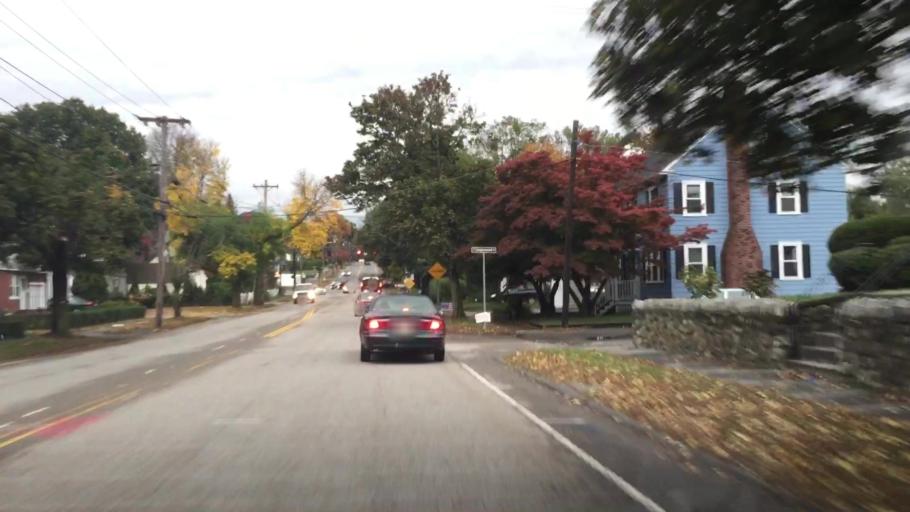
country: US
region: Massachusetts
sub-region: Essex County
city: North Andover
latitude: 42.6952
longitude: -71.1371
